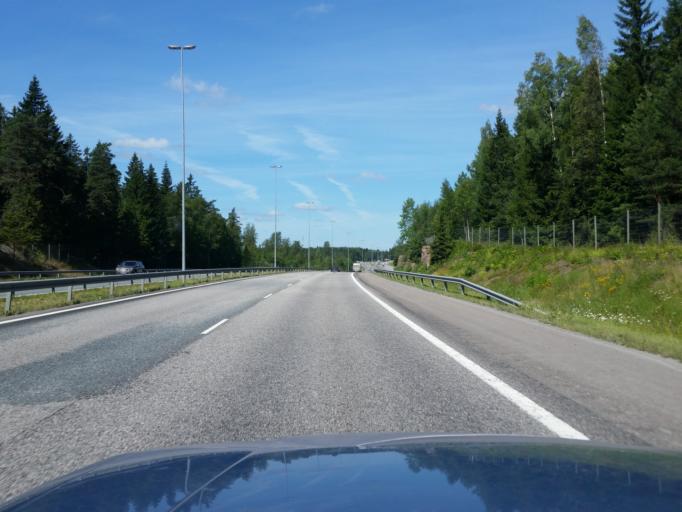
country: FI
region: Uusimaa
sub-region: Helsinki
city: Kirkkonummi
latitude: 60.2674
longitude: 24.4750
